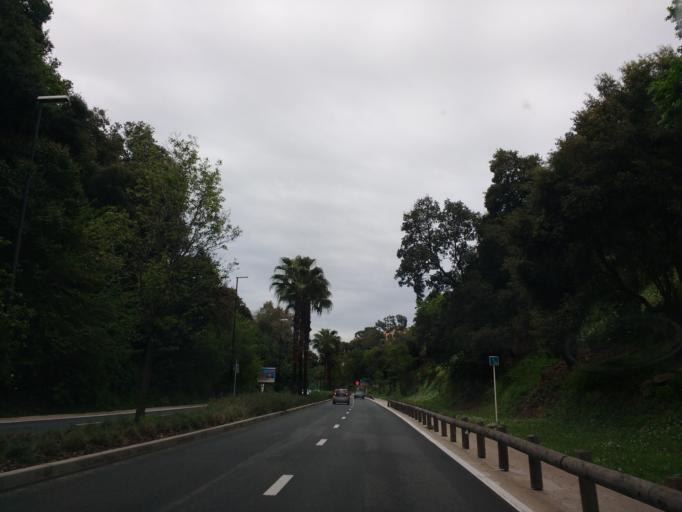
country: FR
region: Provence-Alpes-Cote d'Azur
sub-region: Departement des Alpes-Maritimes
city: Cannes
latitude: 43.5590
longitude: 7.0020
